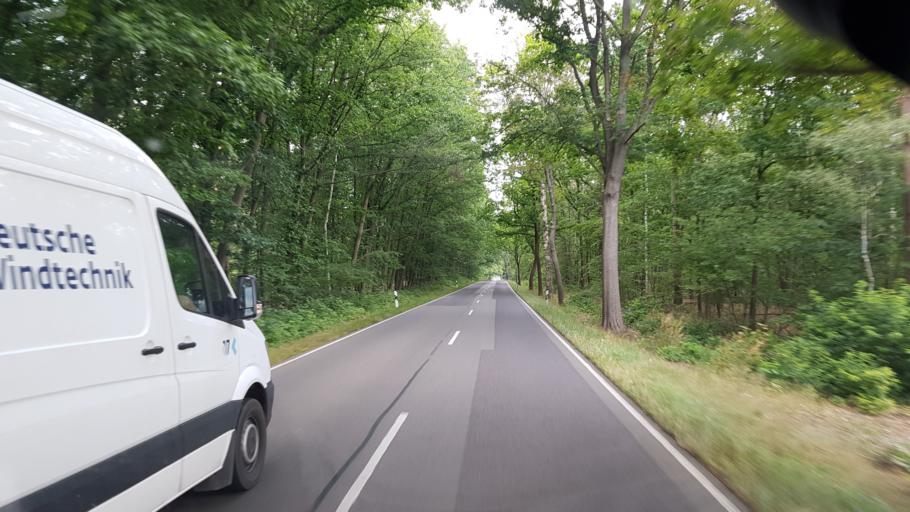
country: DE
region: Brandenburg
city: Lebusa
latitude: 51.8078
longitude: 13.4221
